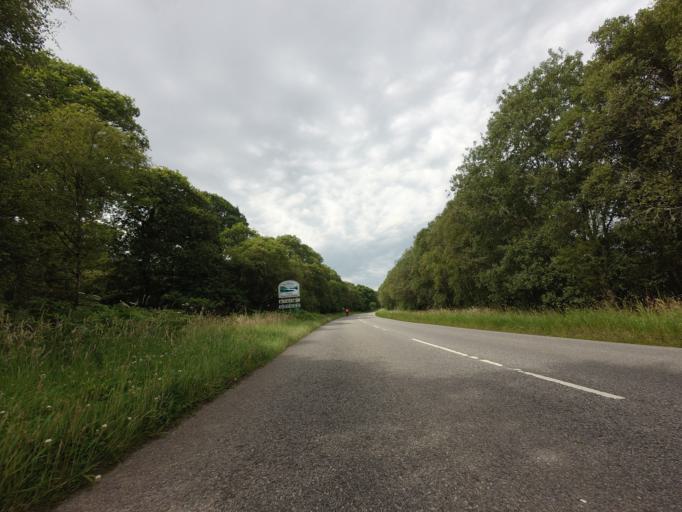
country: GB
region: Scotland
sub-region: Highland
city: Alness
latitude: 57.8755
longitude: -4.3567
